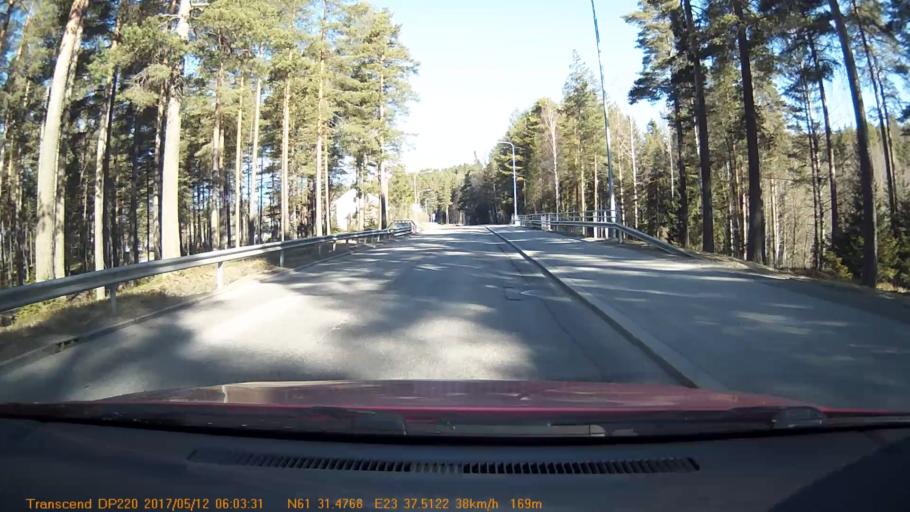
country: FI
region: Pirkanmaa
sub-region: Tampere
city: Yloejaervi
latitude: 61.5246
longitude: 23.6253
